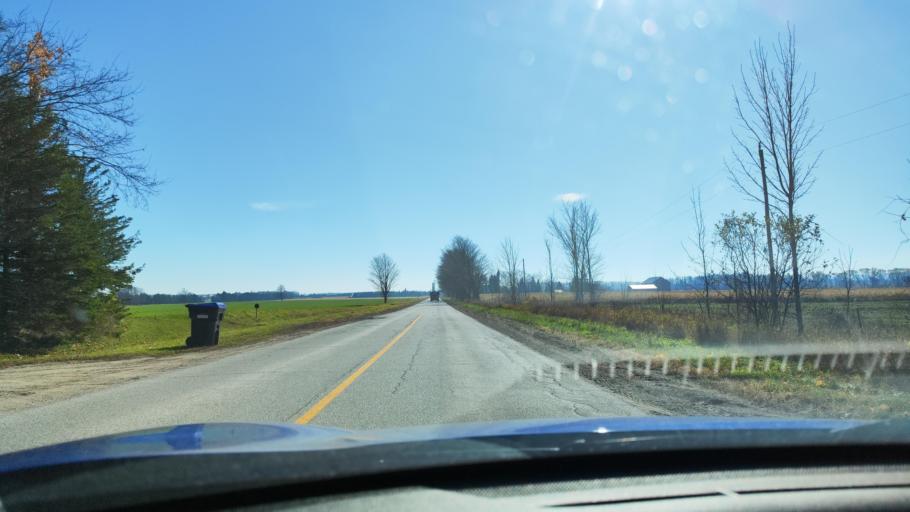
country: CA
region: Ontario
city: Wasaga Beach
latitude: 44.4544
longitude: -80.0019
